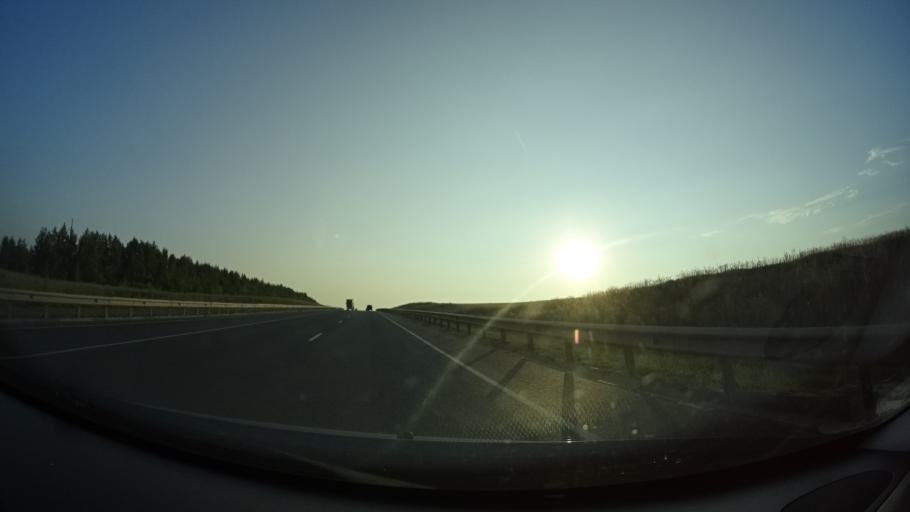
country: RU
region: Samara
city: Isakly
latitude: 54.0205
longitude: 51.8169
